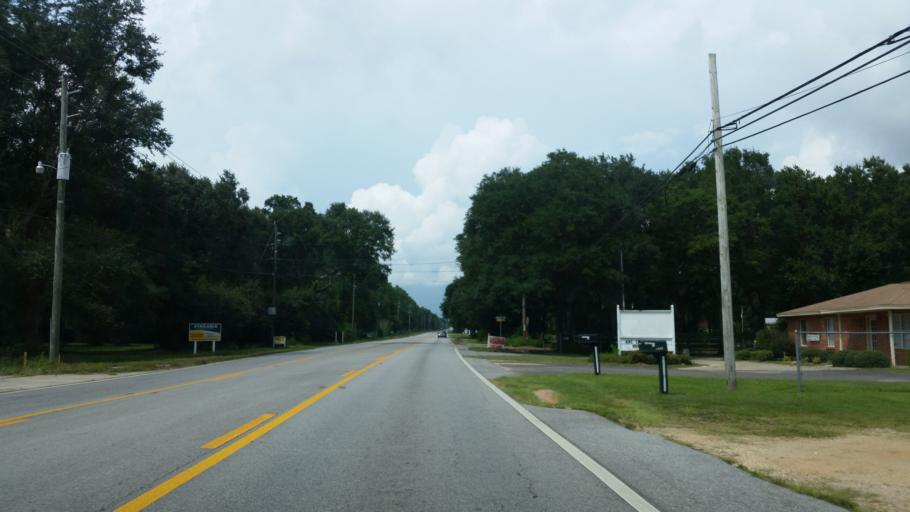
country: US
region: Florida
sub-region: Santa Rosa County
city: Pace
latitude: 30.6069
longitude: -87.1822
